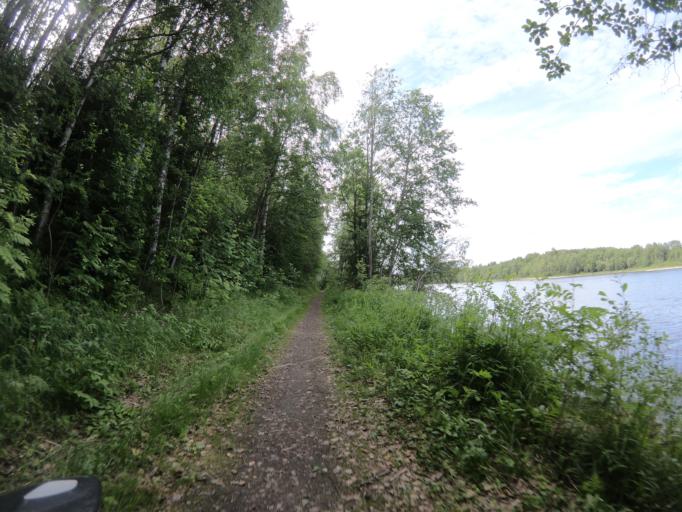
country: SE
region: Vaesterbotten
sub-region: Umea Kommun
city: Roback
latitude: 63.8192
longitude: 20.2182
